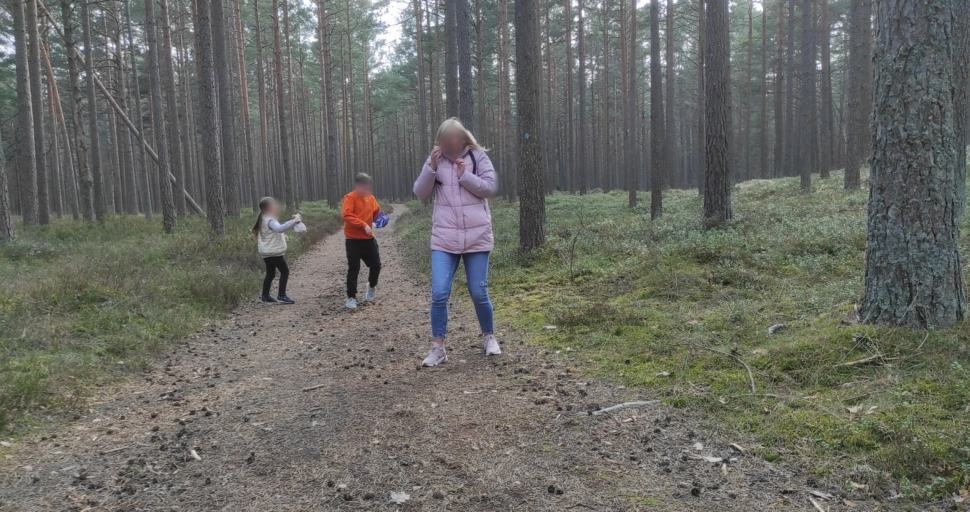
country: LV
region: Nica
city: Nica
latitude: 56.3337
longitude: 20.9895
